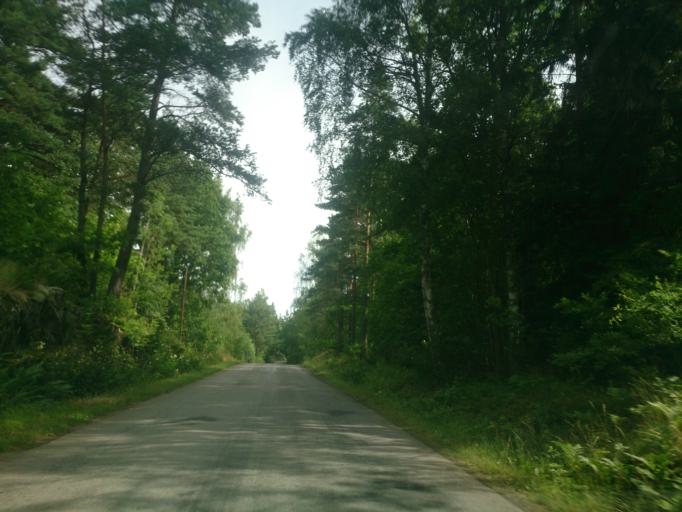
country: SE
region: OEstergoetland
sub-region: Soderkopings Kommun
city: Soederkoeping
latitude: 58.2833
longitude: 16.2302
